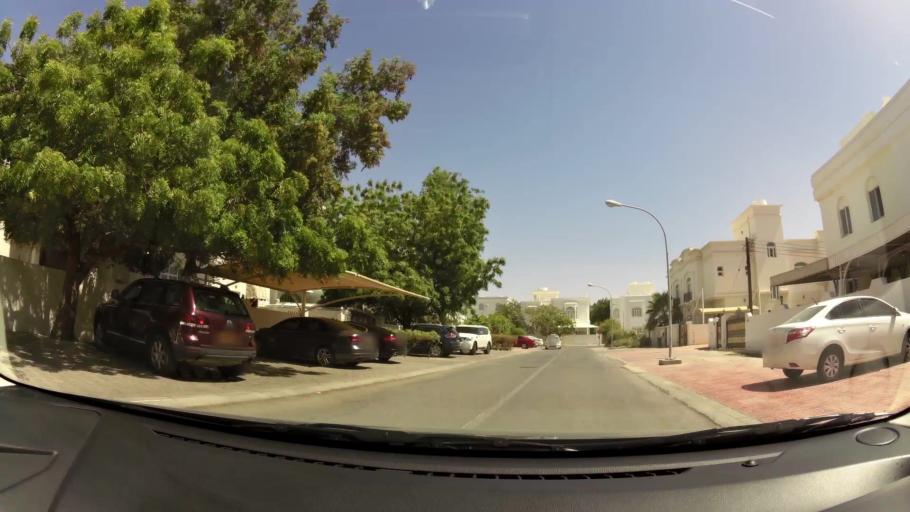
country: OM
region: Muhafazat Masqat
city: Bawshar
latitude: 23.6004
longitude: 58.3597
